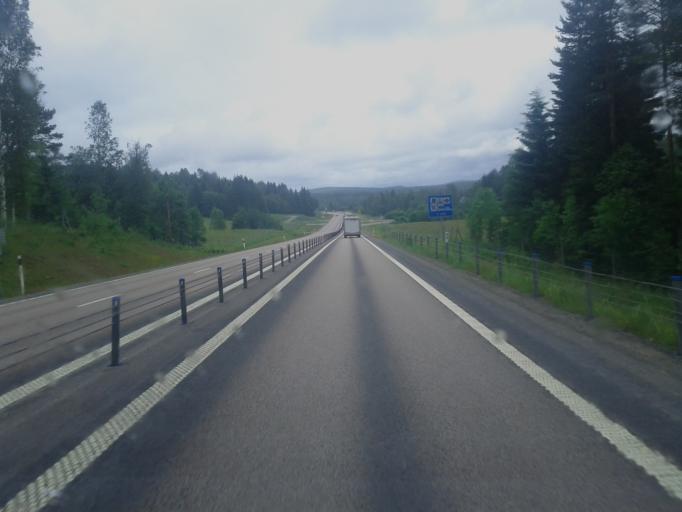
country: SE
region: Vaesternorrland
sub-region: Timra Kommun
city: Soraker
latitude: 62.5519
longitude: 17.6251
